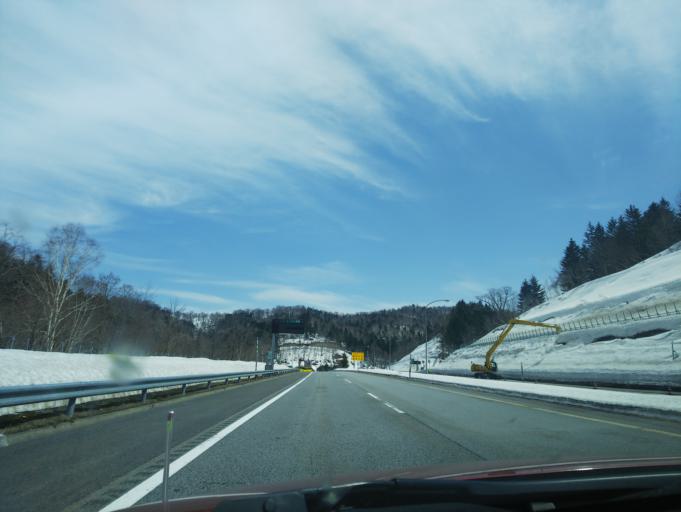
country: JP
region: Hokkaido
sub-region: Asahikawa-shi
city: Asahikawa
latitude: 43.7810
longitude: 142.2086
